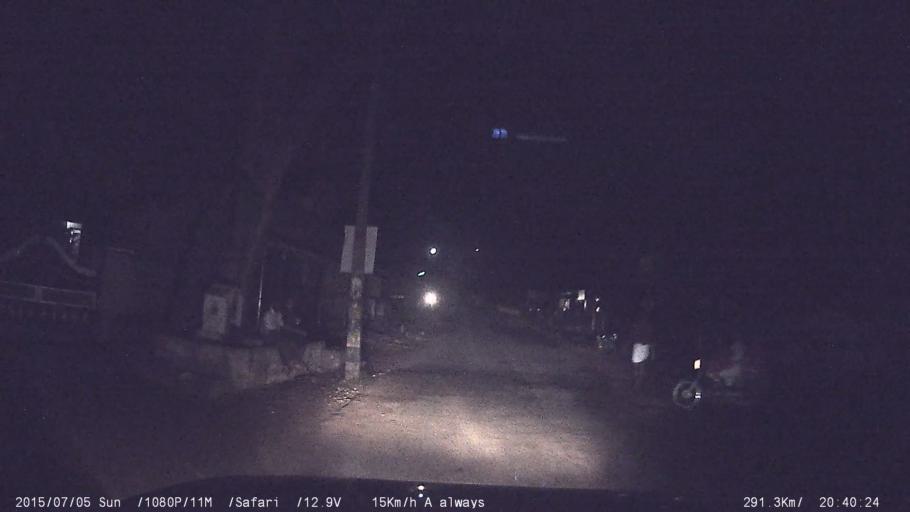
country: IN
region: Kerala
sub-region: Palakkad district
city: Mannarakkat
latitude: 10.9933
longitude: 76.5024
